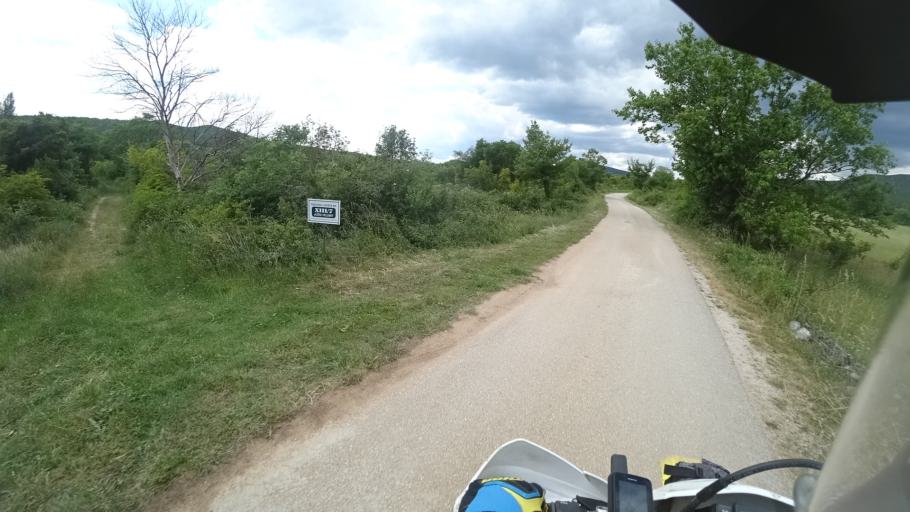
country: HR
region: Sibensko-Kniniska
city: Kistanje
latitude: 44.0923
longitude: 16.0333
